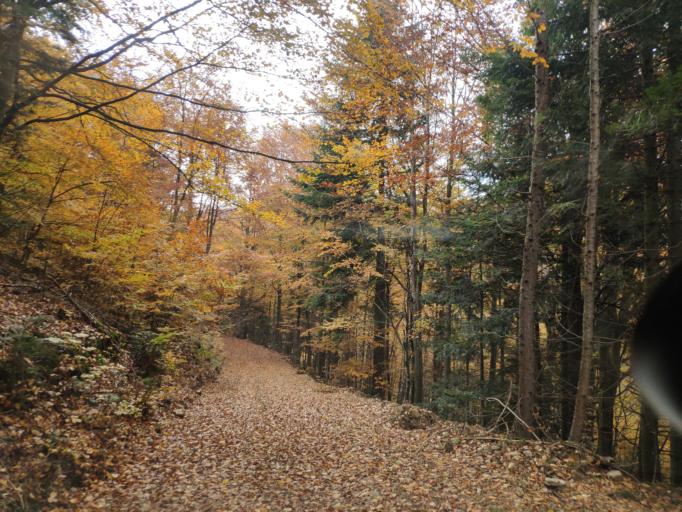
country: SK
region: Kosicky
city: Medzev
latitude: 48.7595
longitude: 20.9759
